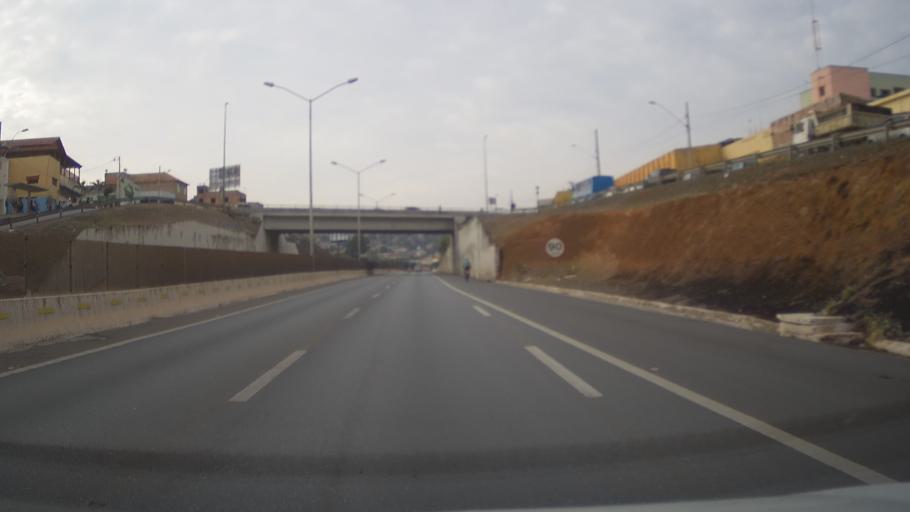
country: BR
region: Minas Gerais
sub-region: Vespasiano
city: Vespasiano
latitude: -19.7503
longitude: -43.9495
